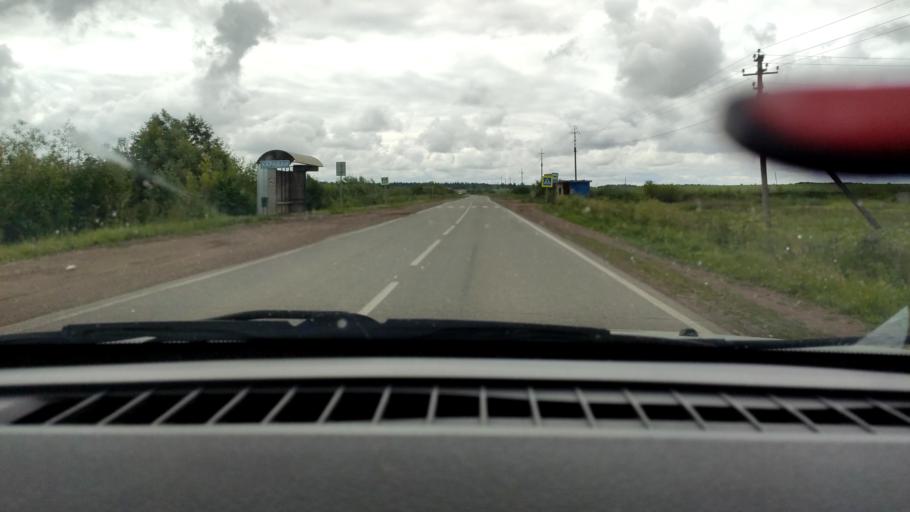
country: RU
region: Perm
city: Ust'-Kachka
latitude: 58.0804
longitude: 55.6169
